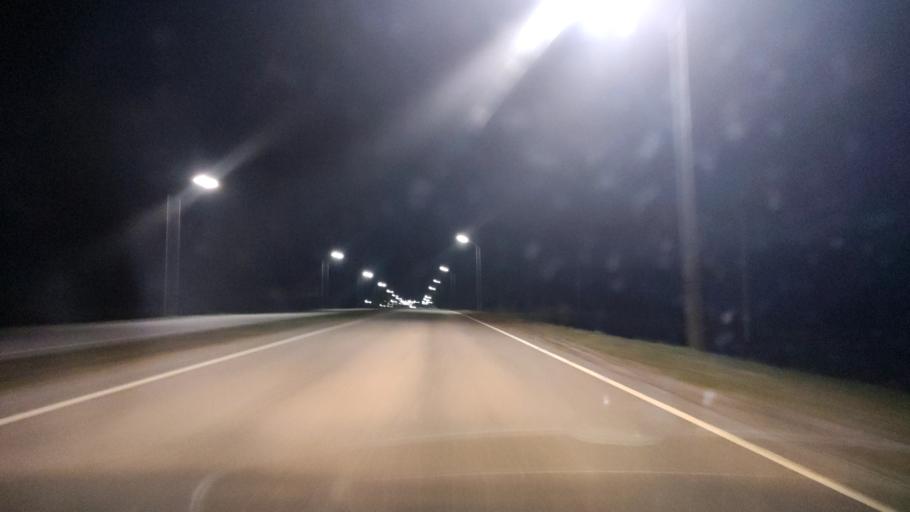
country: RU
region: Belgorod
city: Staryy Oskol
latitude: 51.3854
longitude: 37.8600
